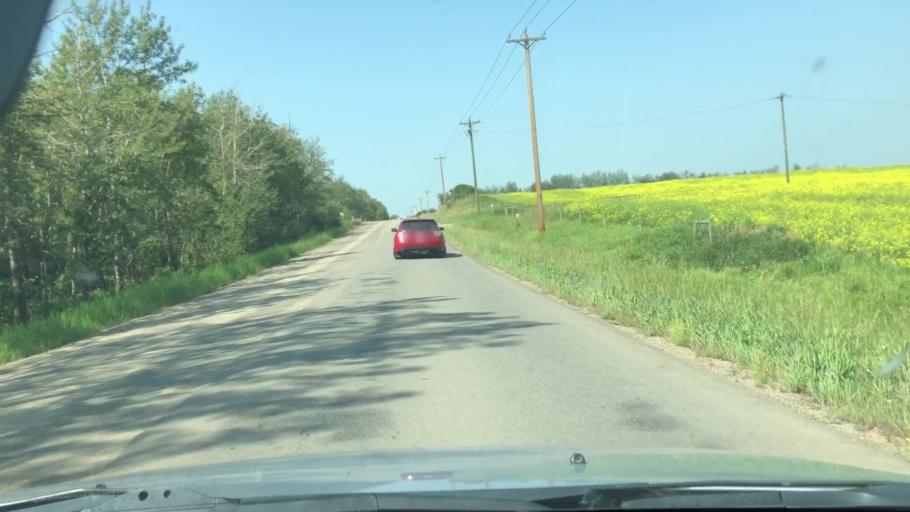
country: CA
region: Alberta
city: Devon
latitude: 53.5122
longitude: -113.7453
